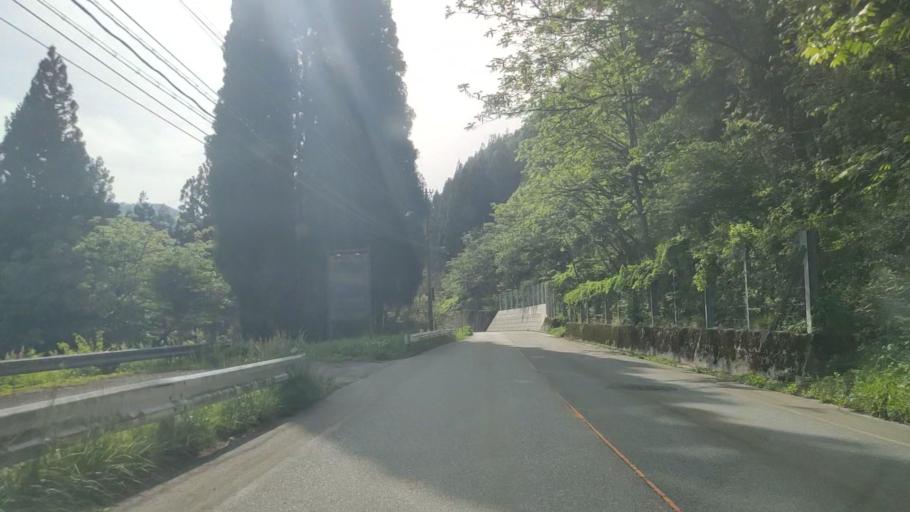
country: JP
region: Gifu
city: Takayama
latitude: 36.2973
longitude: 137.3599
